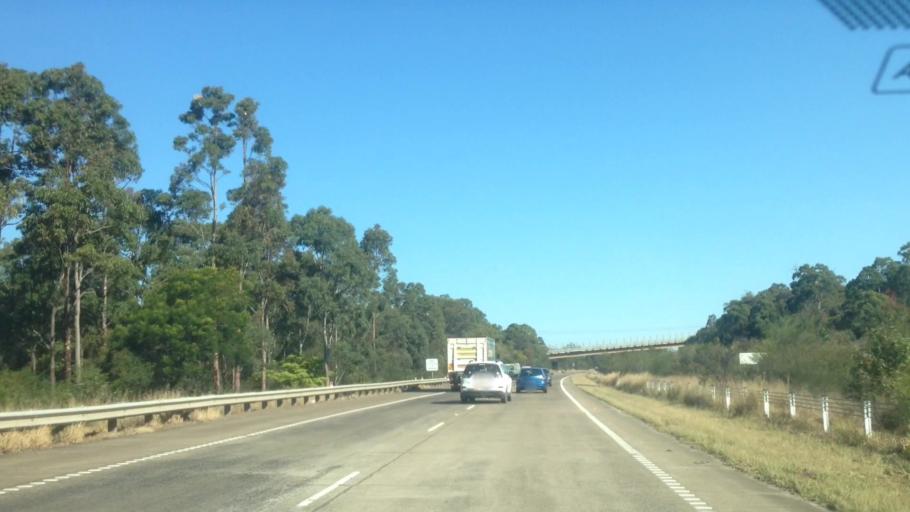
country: AU
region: New South Wales
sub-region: Wyong Shire
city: Charmhaven
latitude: -33.1904
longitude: 151.4673
